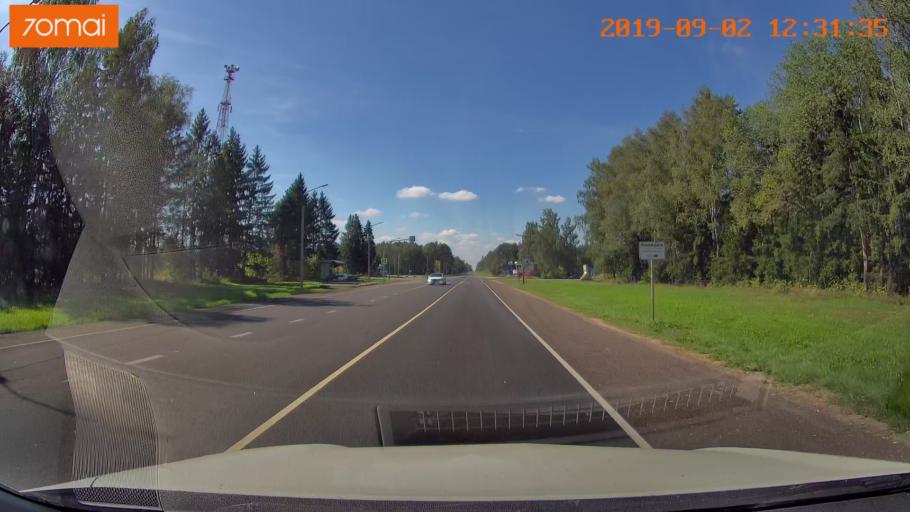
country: RU
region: Smolensk
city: Shumyachi
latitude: 53.8234
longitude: 32.4466
